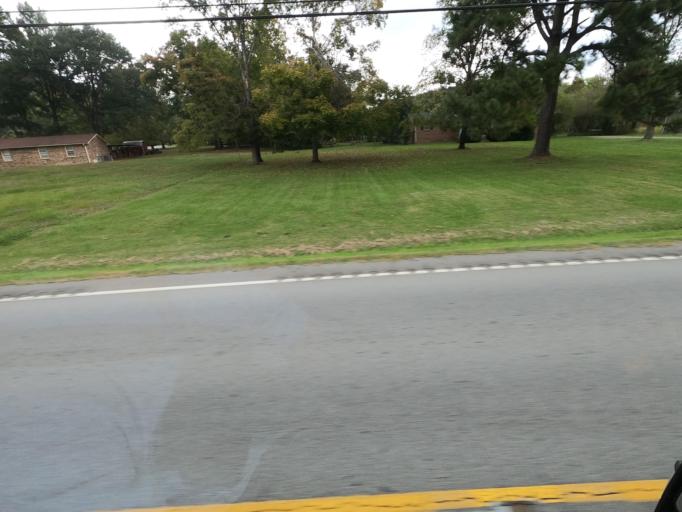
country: US
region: Tennessee
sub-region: Cheatham County
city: Pegram
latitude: 36.1049
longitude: -87.0588
